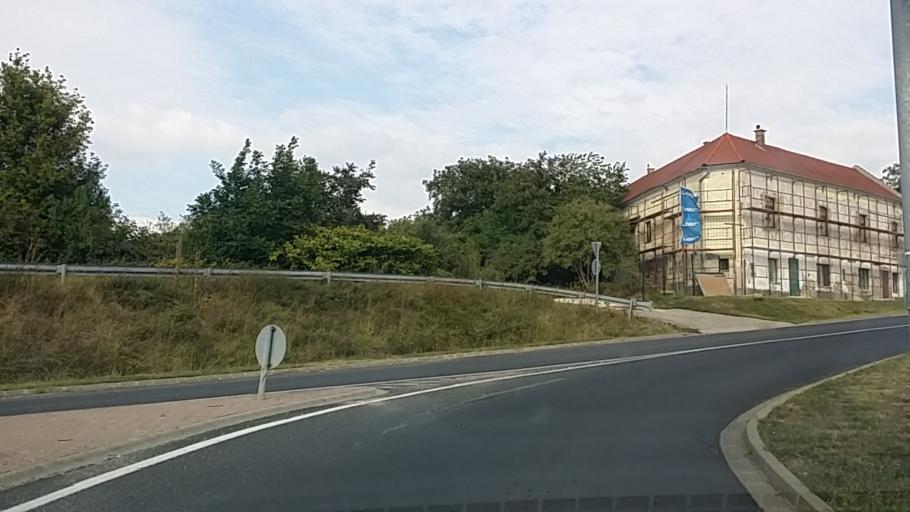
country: HU
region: Gyor-Moson-Sopron
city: Sopron
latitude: 47.6821
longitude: 16.6138
